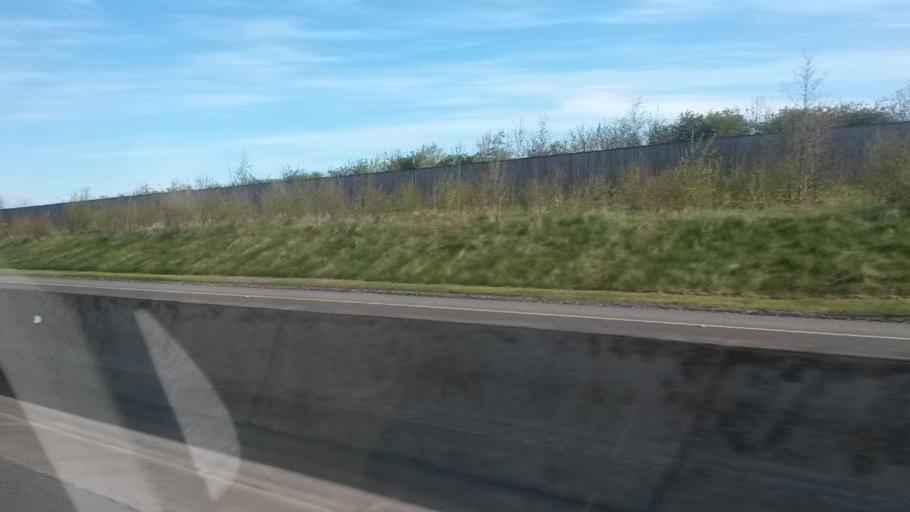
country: IE
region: Leinster
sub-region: An Mhi
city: Navan
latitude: 53.6045
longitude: -6.6441
